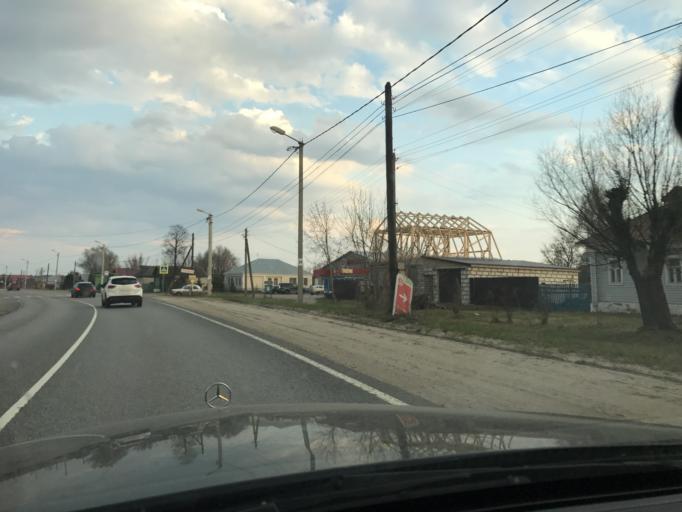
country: RU
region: Vladimir
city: Murom
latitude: 55.6104
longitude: 41.9515
